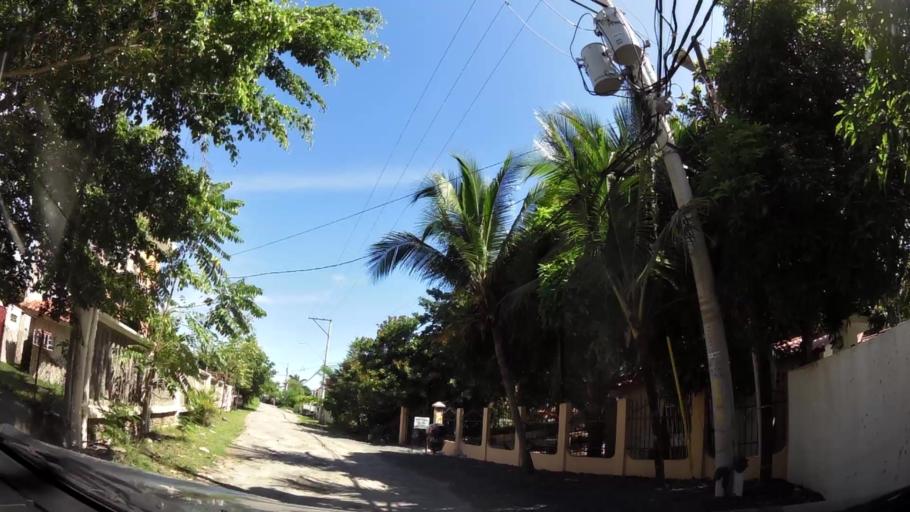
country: PA
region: Panama
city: Nueva Gorgona
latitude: 8.5554
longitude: -79.8616
